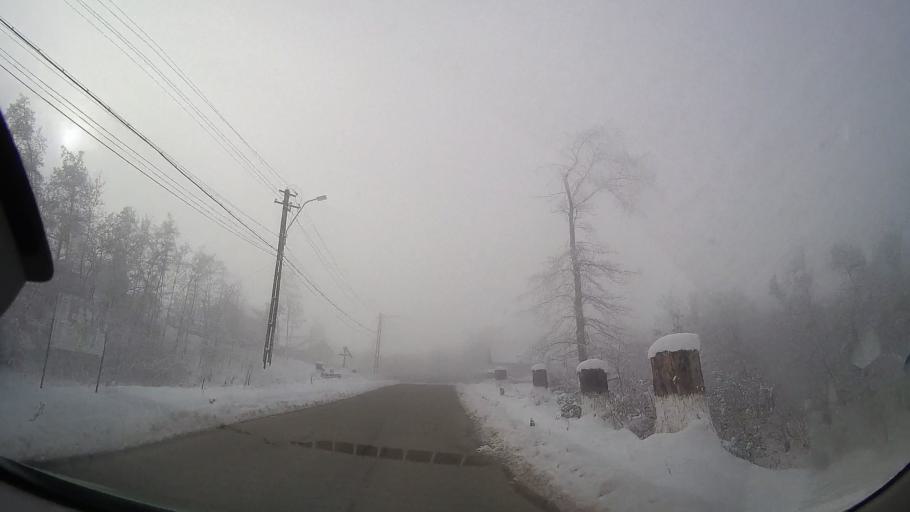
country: RO
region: Iasi
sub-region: Comuna Valea Seaca
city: Topile
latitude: 47.2607
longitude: 26.6677
